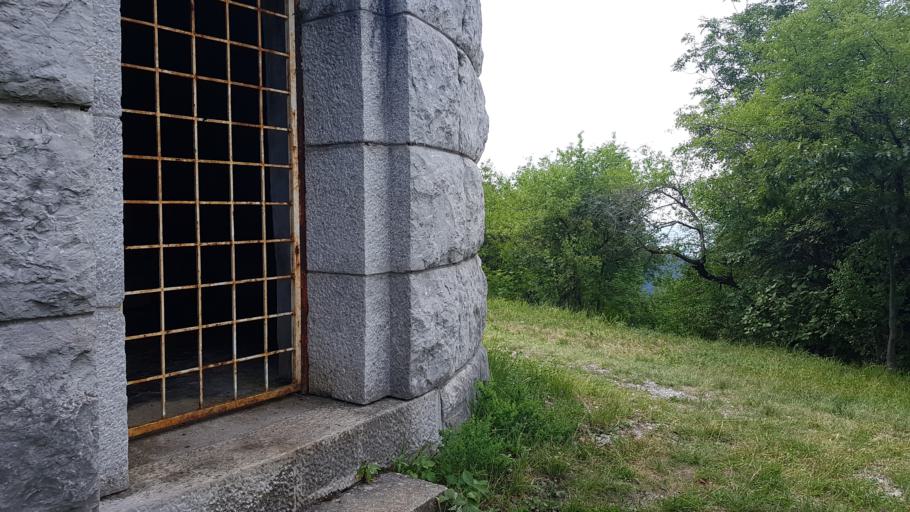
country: SI
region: Kanal
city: Deskle
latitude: 46.0145
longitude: 13.6363
